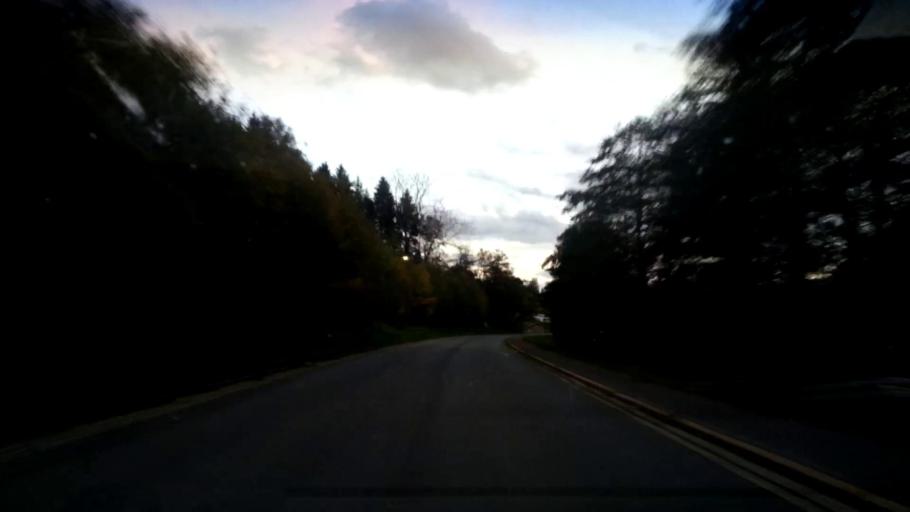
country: DE
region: Bavaria
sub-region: Upper Franconia
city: Warmensteinach
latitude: 50.0007
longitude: 11.7903
